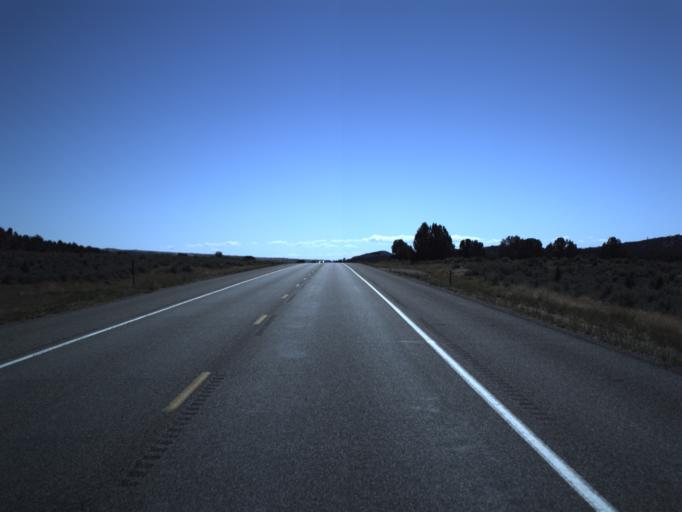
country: US
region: Utah
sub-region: Washington County
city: Ivins
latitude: 37.2823
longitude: -113.6540
